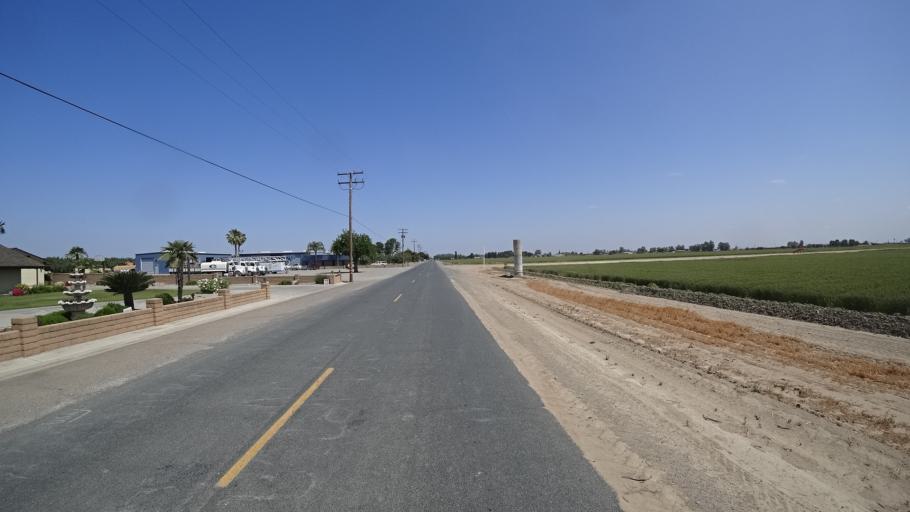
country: US
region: California
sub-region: Kings County
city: Home Garden
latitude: 36.2904
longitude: -119.6190
